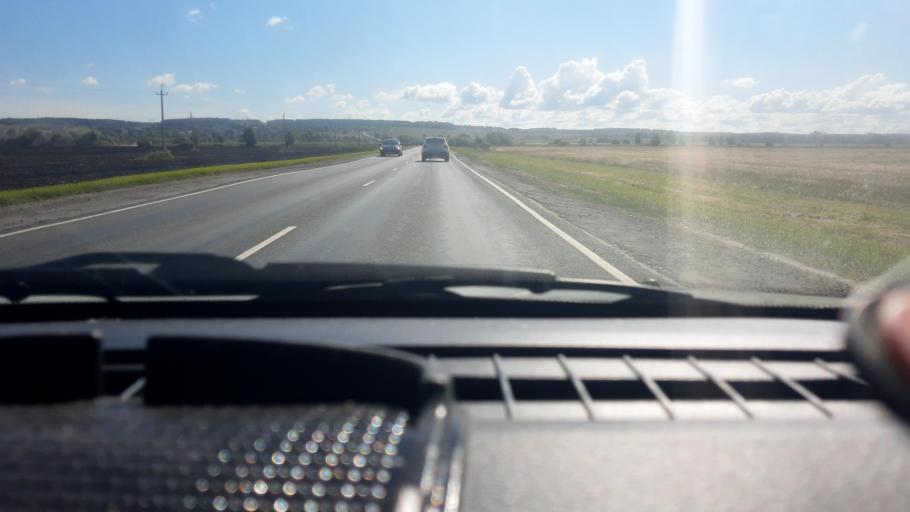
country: RU
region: Nizjnij Novgorod
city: Kstovo
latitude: 56.0150
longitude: 44.1937
